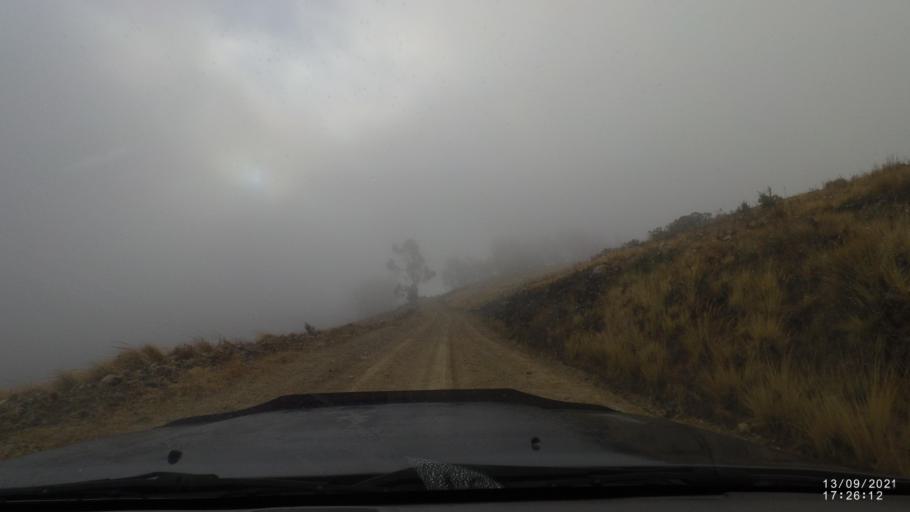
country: BO
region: Cochabamba
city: Colomi
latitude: -17.3610
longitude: -65.7839
